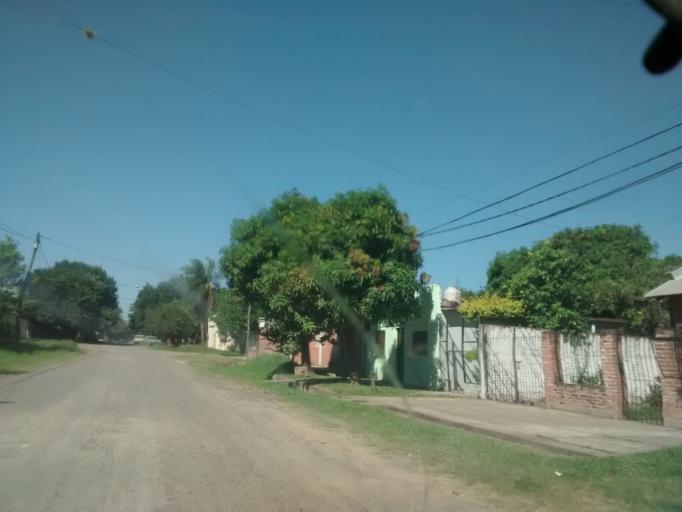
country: AR
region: Chaco
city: Resistencia
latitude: -27.4403
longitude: -58.9727
